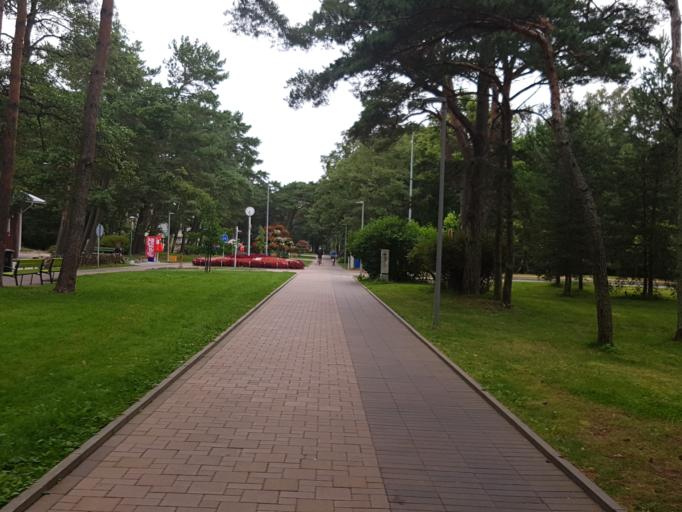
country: LT
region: Klaipedos apskritis
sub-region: Klaipeda
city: Palanga
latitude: 55.9153
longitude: 21.0526
